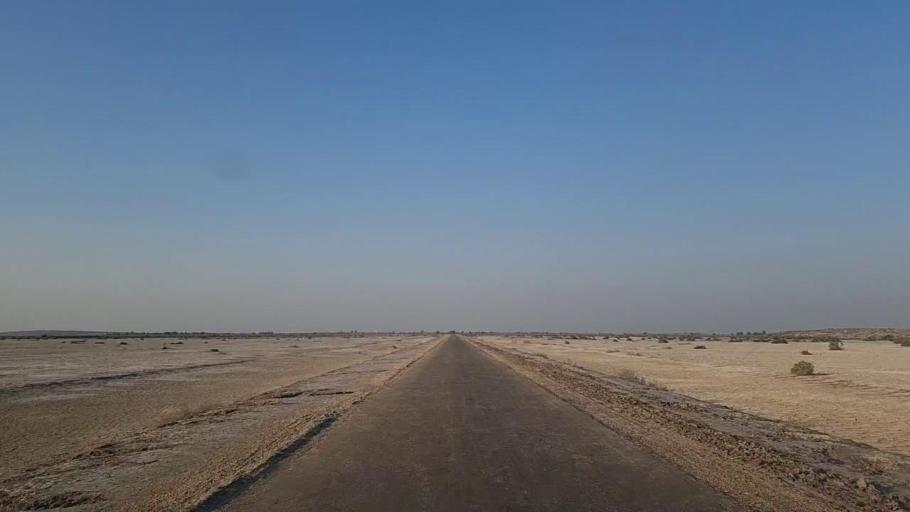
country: PK
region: Sindh
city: Jam Sahib
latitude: 26.3150
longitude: 68.6688
